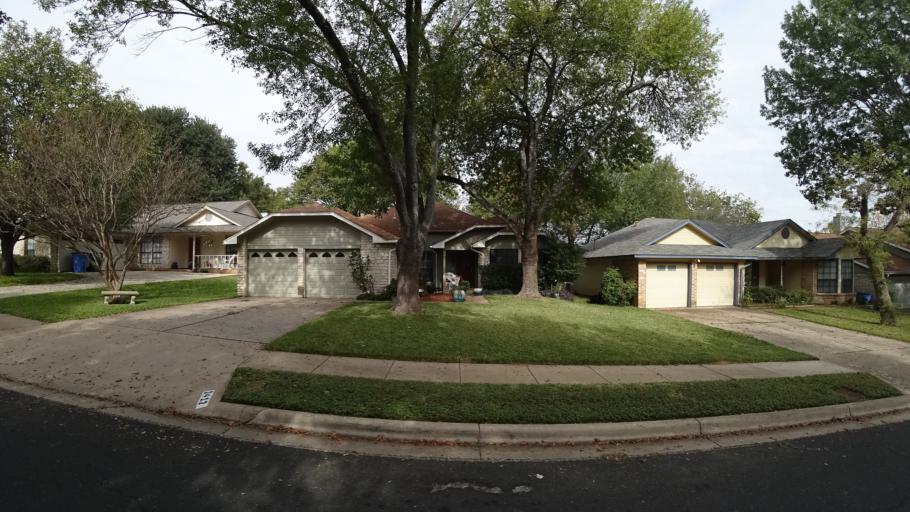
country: US
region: Texas
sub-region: Travis County
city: Wells Branch
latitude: 30.4460
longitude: -97.6837
